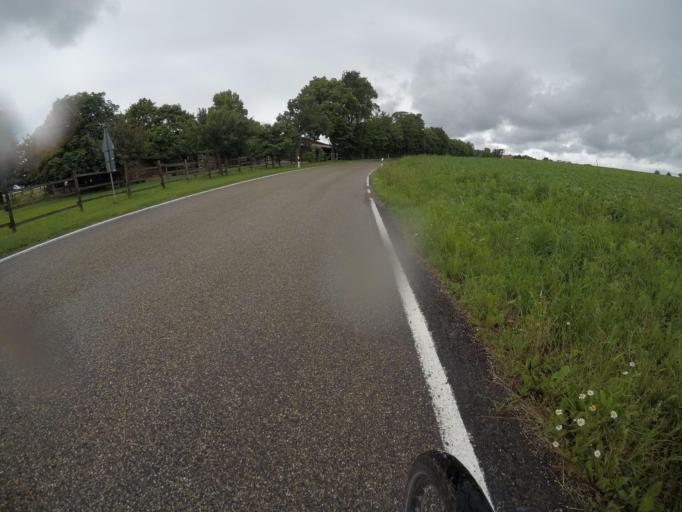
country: DE
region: Baden-Wuerttemberg
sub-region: Regierungsbezirk Stuttgart
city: Unterjettingen
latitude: 48.5673
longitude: 8.8205
